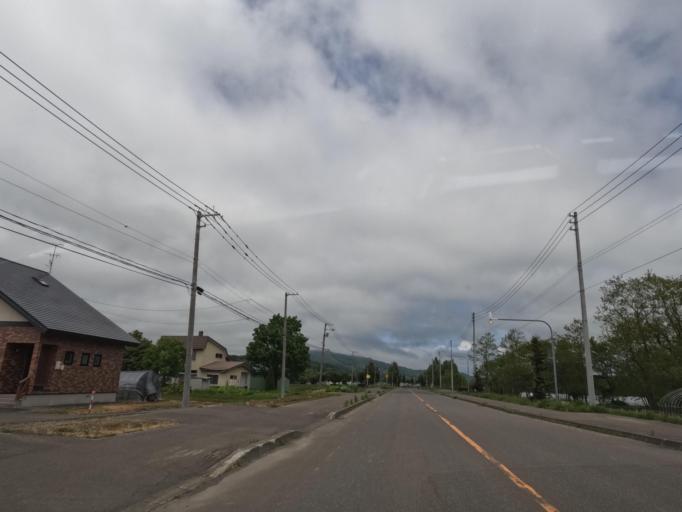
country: JP
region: Hokkaido
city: Tobetsu
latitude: 43.2563
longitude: 141.5233
